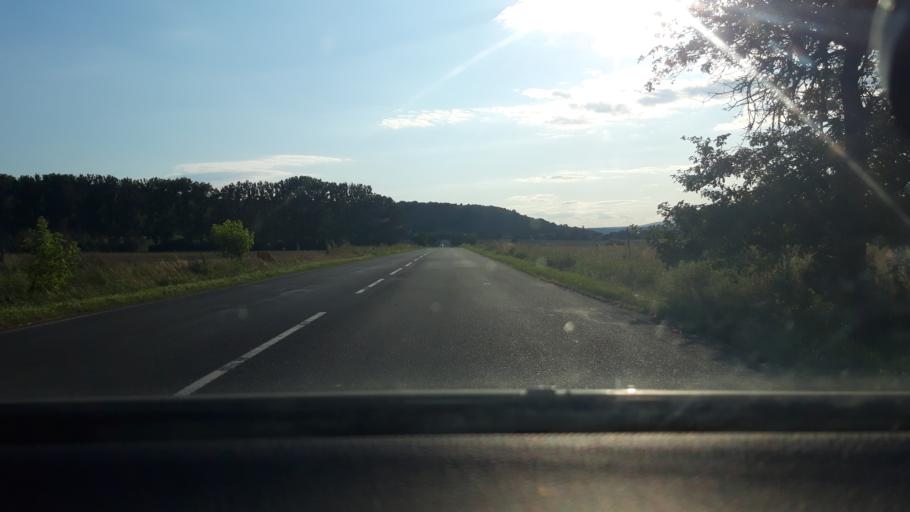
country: SK
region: Banskobystricky
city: Fil'akovo
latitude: 48.2904
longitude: 19.7663
